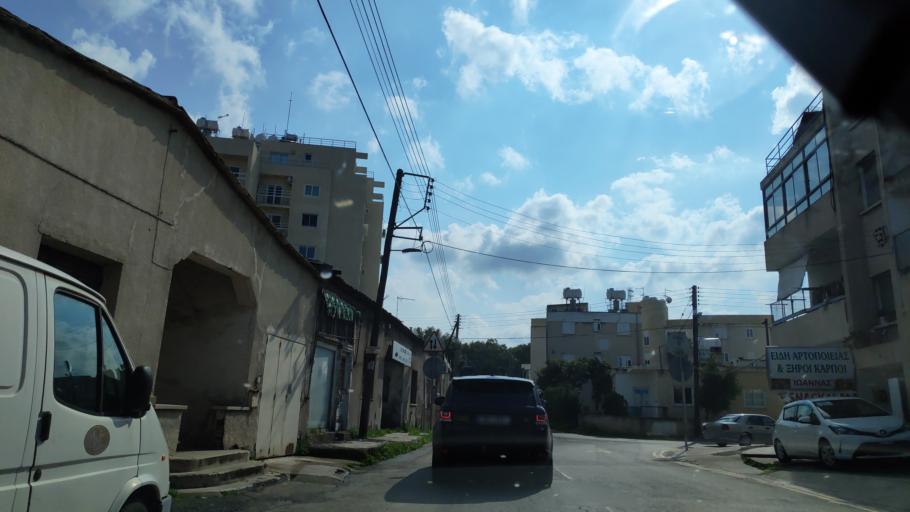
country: CY
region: Lefkosia
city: Nicosia
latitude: 35.1451
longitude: 33.3402
